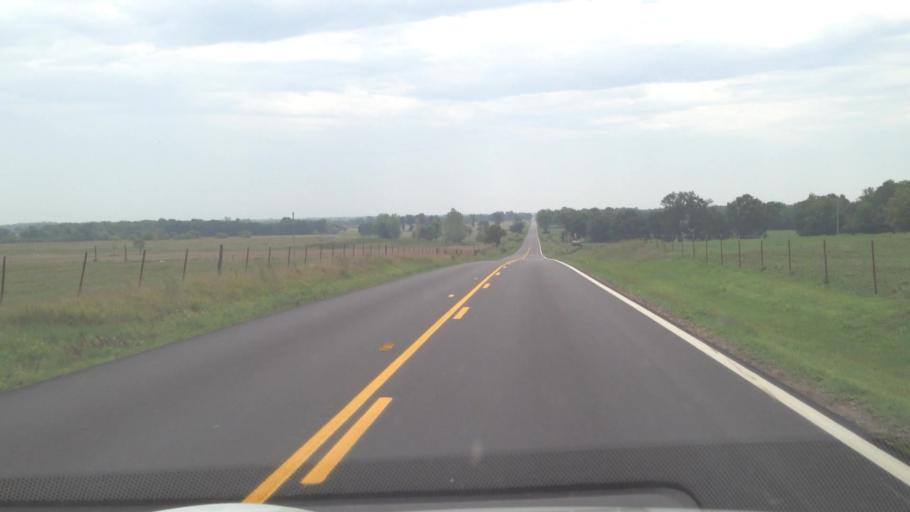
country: US
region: Kansas
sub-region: Crawford County
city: Girard
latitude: 37.5454
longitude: -94.9605
